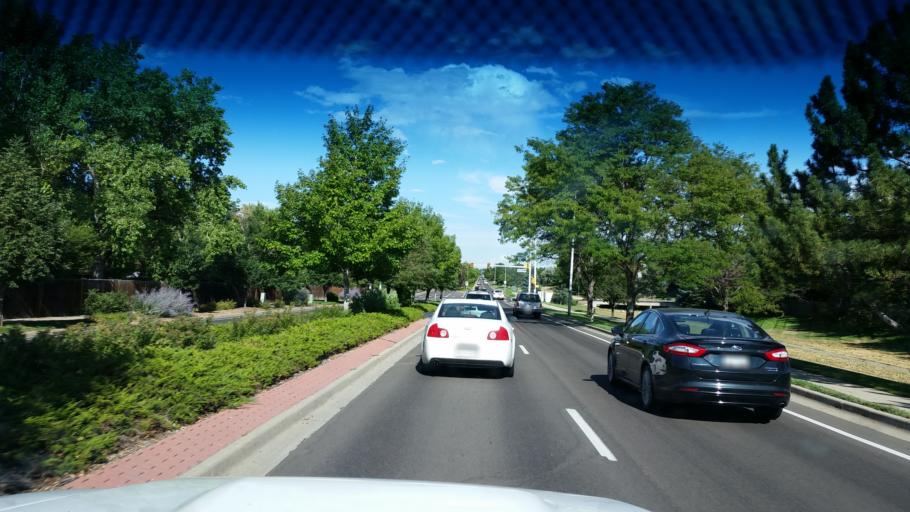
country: US
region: Colorado
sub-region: Broomfield County
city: Broomfield
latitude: 39.9286
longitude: -105.0301
